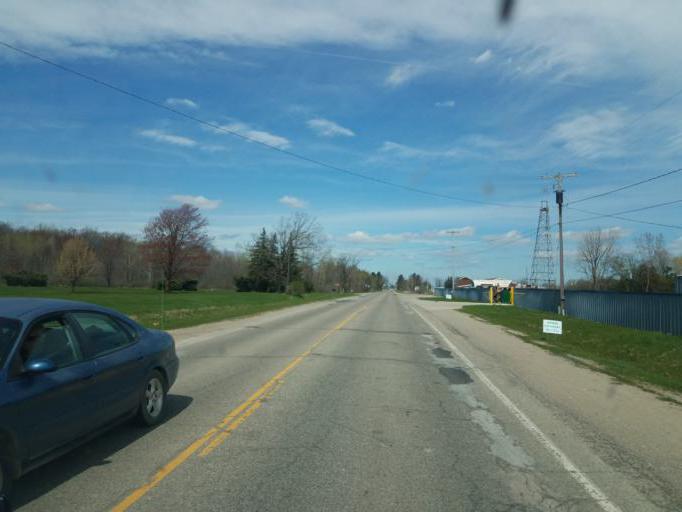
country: US
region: Michigan
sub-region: Isabella County
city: Mount Pleasant
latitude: 43.6321
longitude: -84.7681
